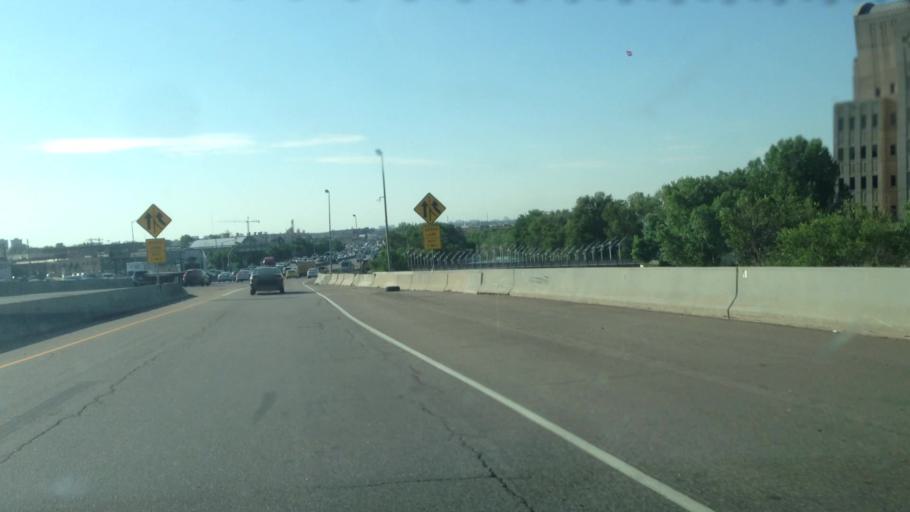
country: US
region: Colorado
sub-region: Denver County
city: Denver
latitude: 39.7224
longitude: -105.0104
